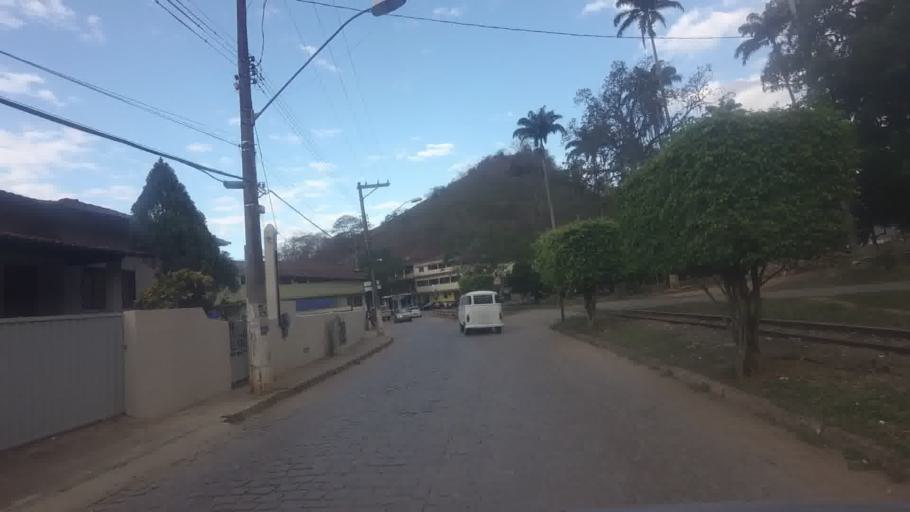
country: BR
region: Espirito Santo
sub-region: Mimoso Do Sul
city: Mimoso do Sul
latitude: -20.9540
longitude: -41.3488
